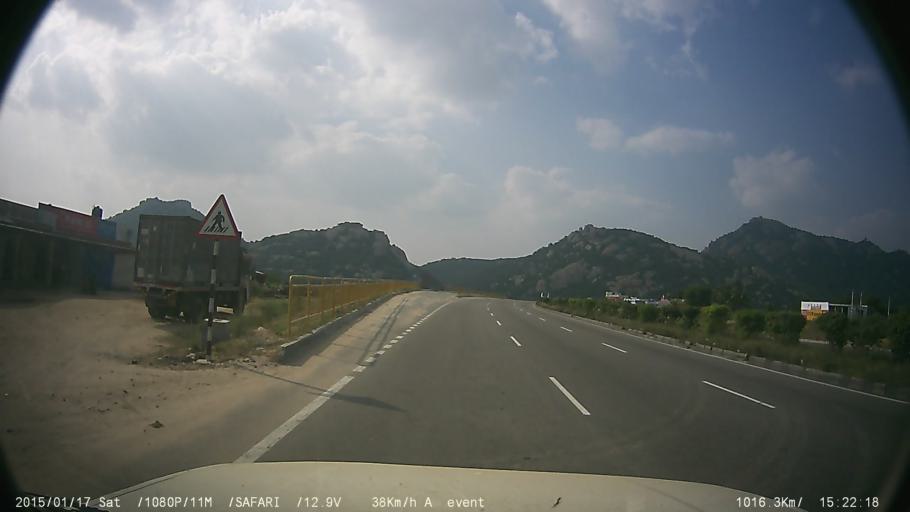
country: IN
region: Tamil Nadu
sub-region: Krishnagiri
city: Krishnagiri
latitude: 12.6021
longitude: 78.1236
